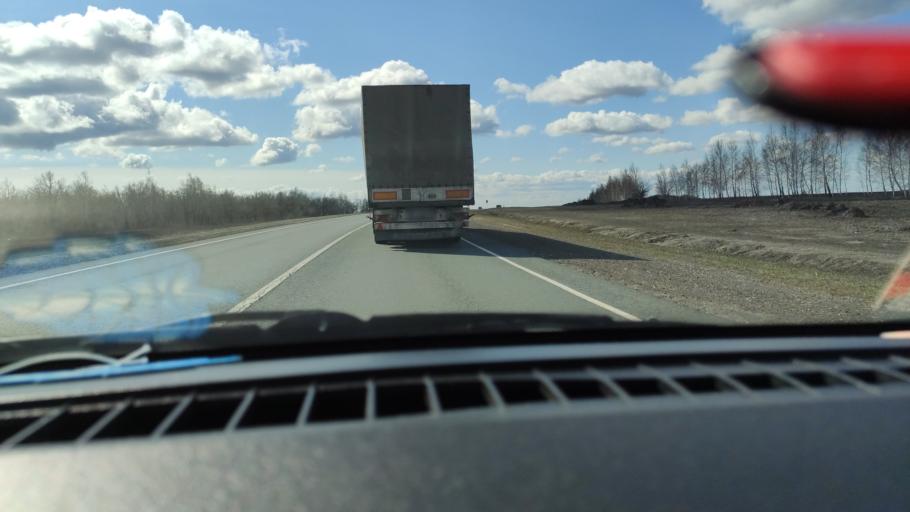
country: RU
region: Samara
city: Syzran'
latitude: 52.9306
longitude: 48.3066
